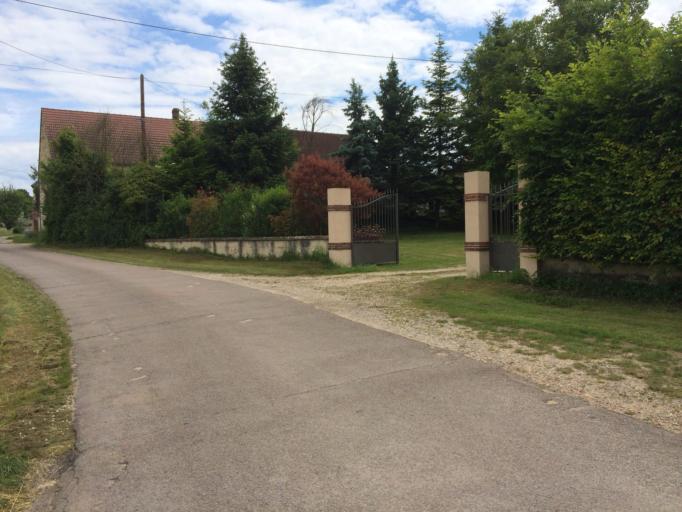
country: FR
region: Bourgogne
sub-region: Departement de l'Yonne
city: Fleury-la-Vallee
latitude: 47.8635
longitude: 3.4083
